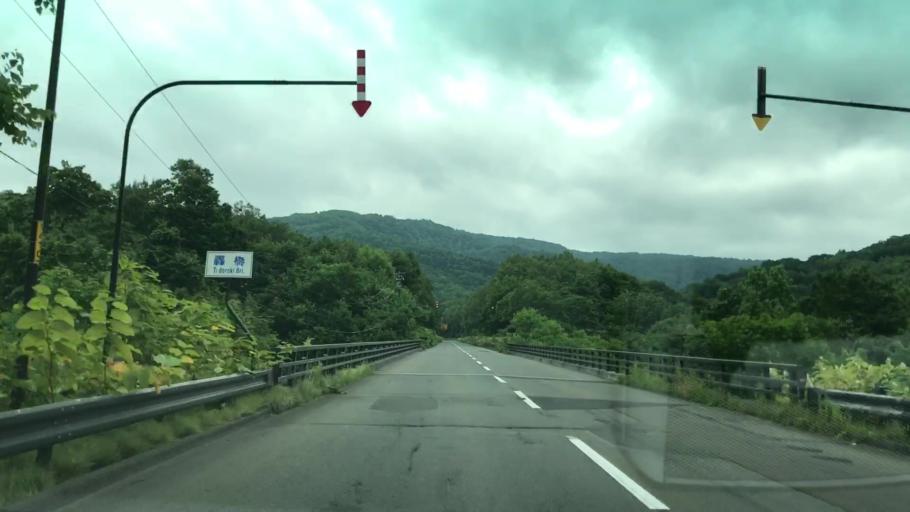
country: JP
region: Hokkaido
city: Yoichi
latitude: 43.0097
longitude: 140.8713
